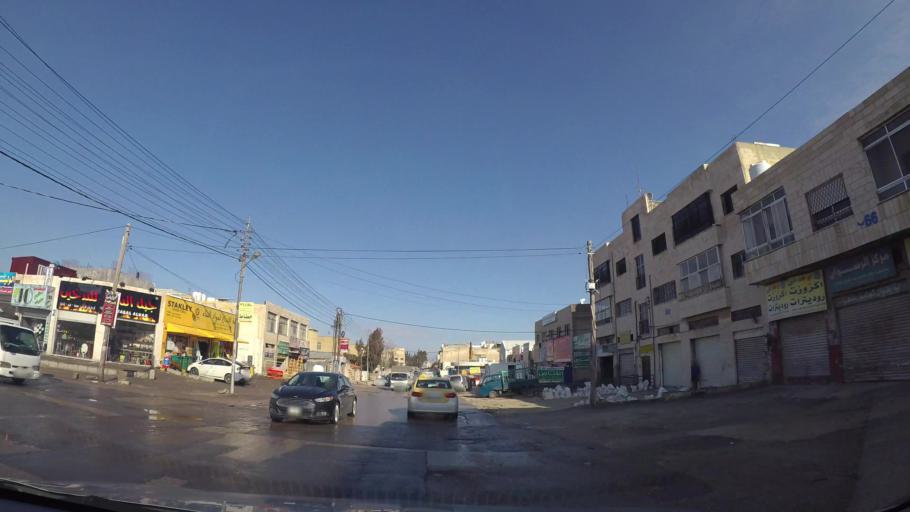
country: JO
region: Amman
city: Al Jubayhah
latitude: 32.0149
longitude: 35.8484
